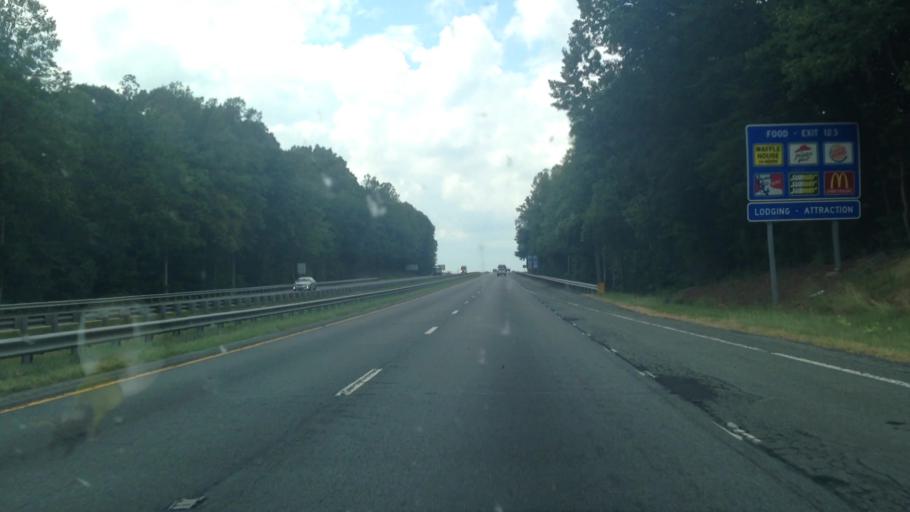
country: US
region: North Carolina
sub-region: Forsyth County
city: Tobaccoville
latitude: 36.2525
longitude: -80.3569
